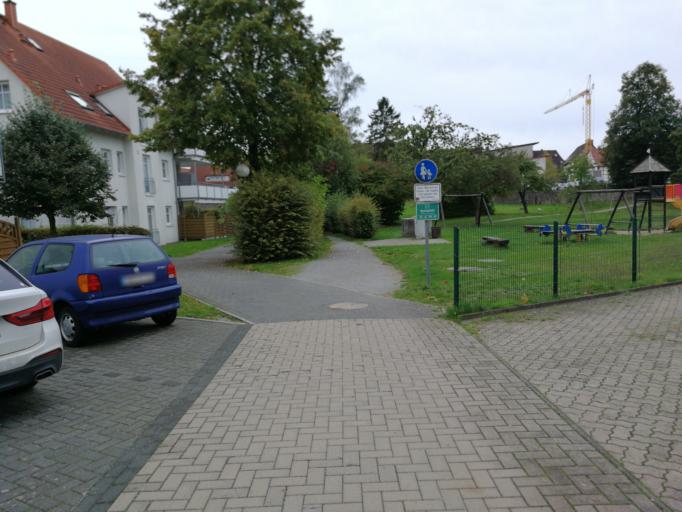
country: DE
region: Lower Saxony
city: Bad Munder am Deister
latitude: 52.1985
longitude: 9.4669
